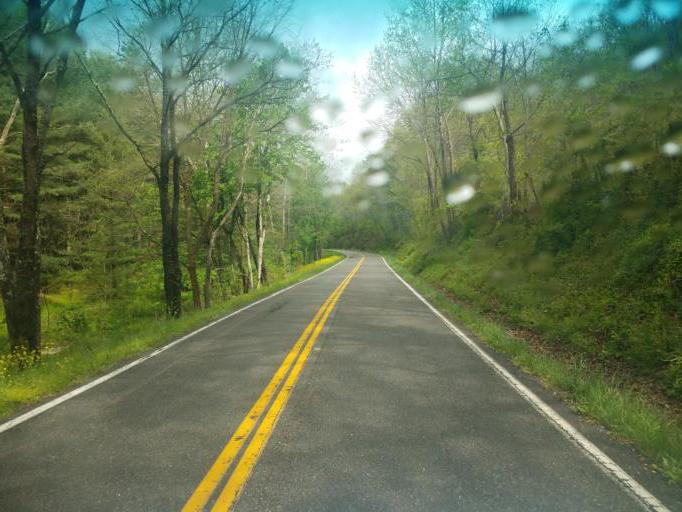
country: US
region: Virginia
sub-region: Smyth County
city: Marion
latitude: 36.9384
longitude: -81.5270
